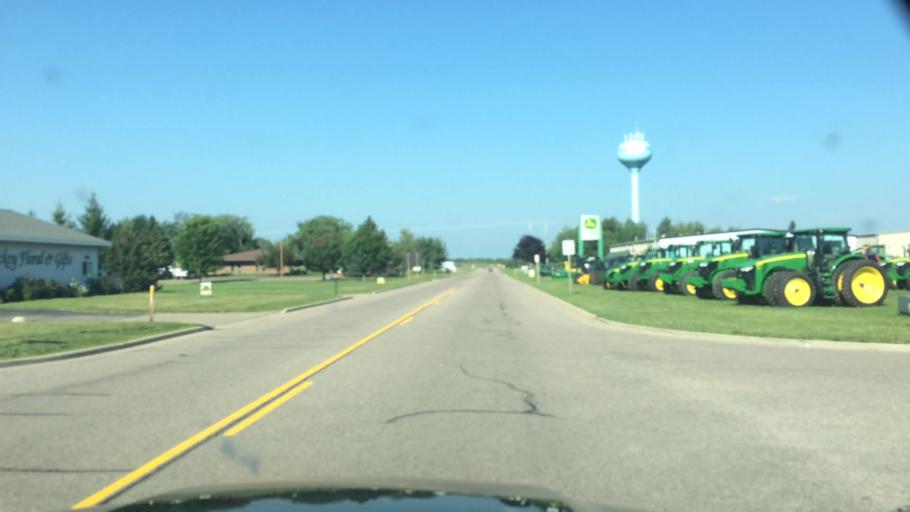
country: US
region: Wisconsin
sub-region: Langlade County
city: Antigo
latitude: 45.1622
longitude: -89.1512
